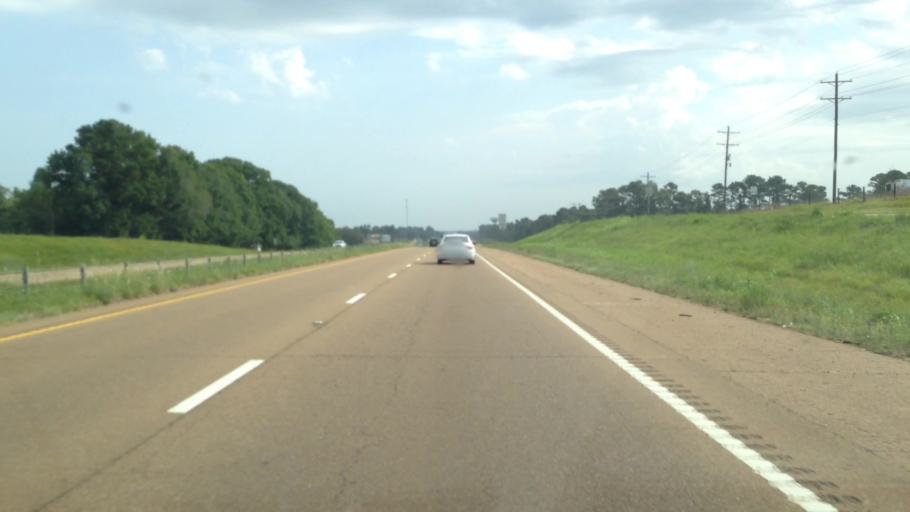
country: US
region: Mississippi
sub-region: Hinds County
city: Terry
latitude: 32.1391
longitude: -90.2832
